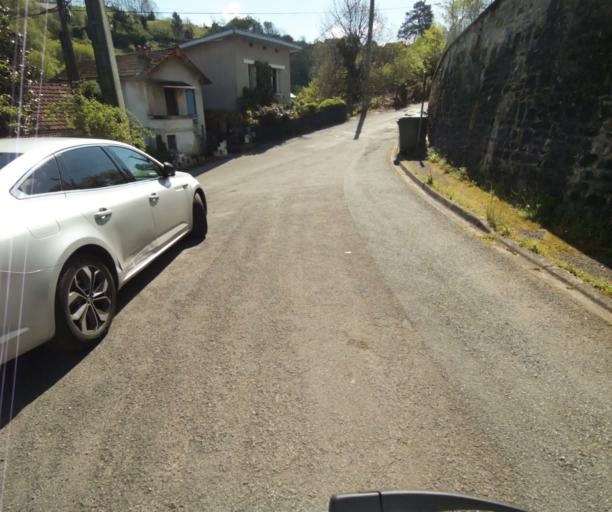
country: FR
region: Limousin
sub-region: Departement de la Correze
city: Tulle
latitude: 45.2677
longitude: 1.7783
